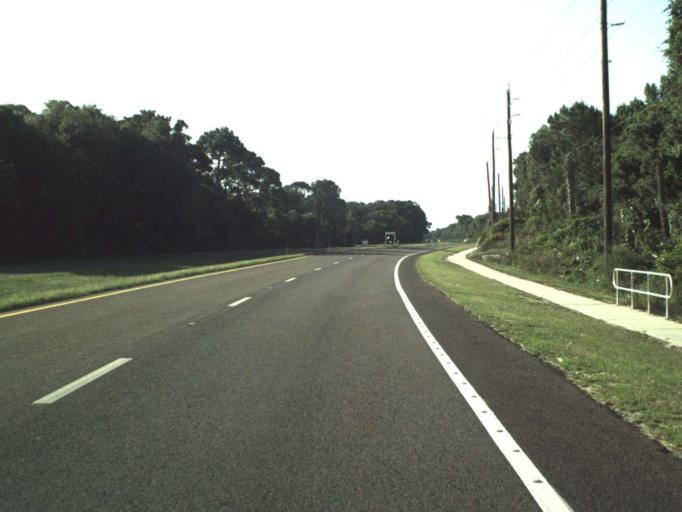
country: US
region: Florida
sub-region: Volusia County
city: Oak Hill
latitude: 28.8482
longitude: -80.8478
